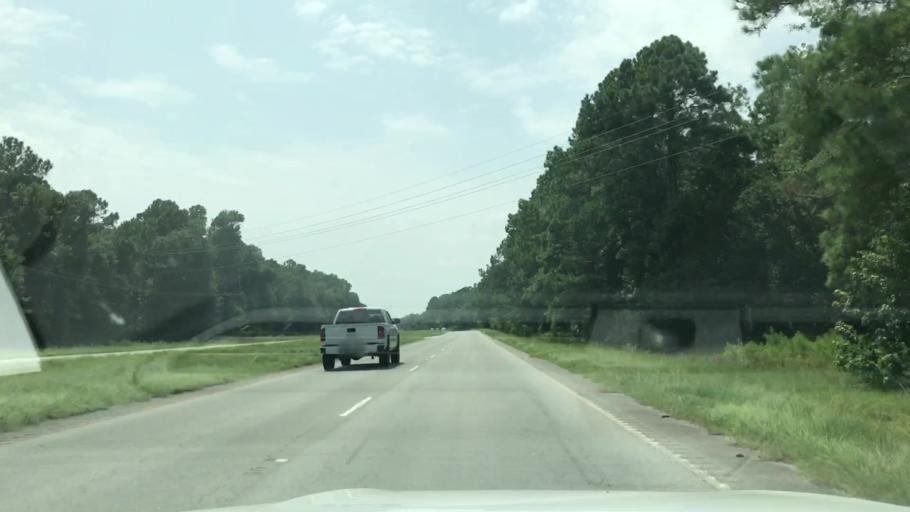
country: US
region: South Carolina
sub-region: Charleston County
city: Awendaw
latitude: 33.0629
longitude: -79.5353
